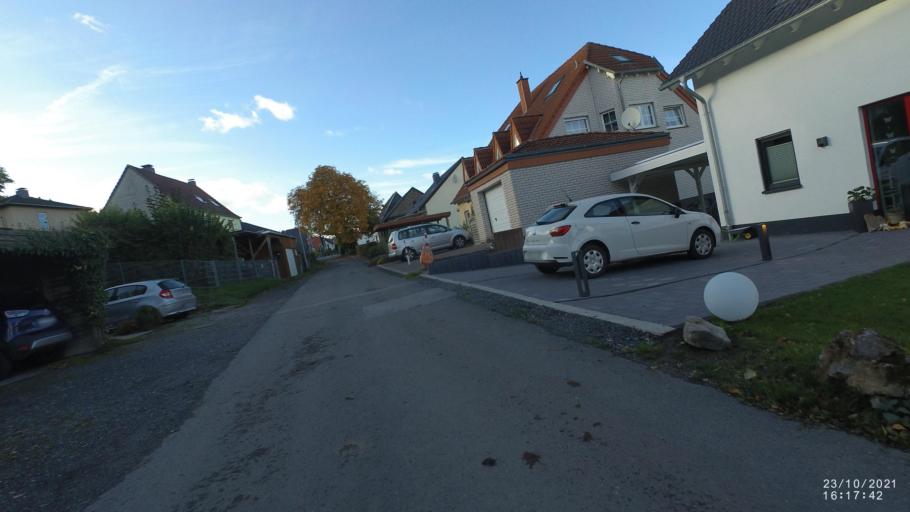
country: DE
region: North Rhine-Westphalia
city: Balve
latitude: 51.3751
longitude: 7.8354
